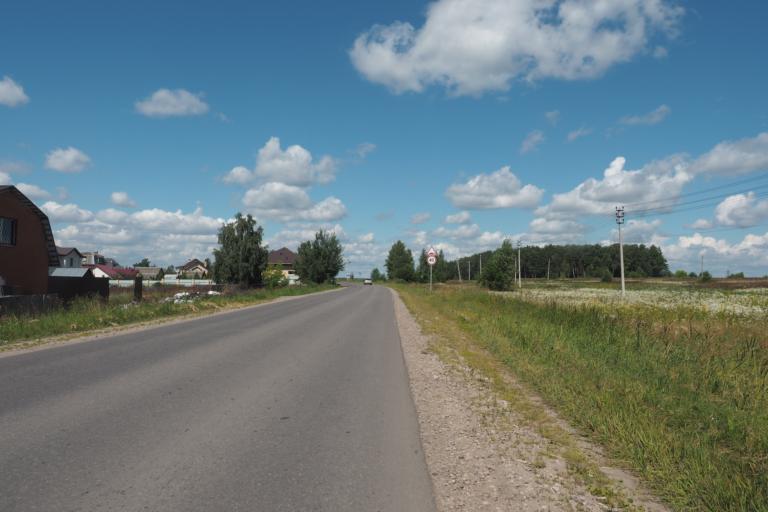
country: RU
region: Moskovskaya
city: Ramenskoye
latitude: 55.5752
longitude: 38.2880
